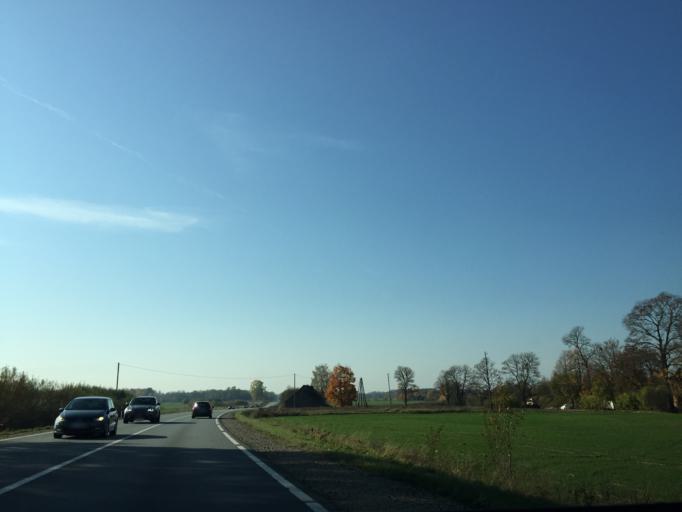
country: LV
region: Dobeles Rajons
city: Dobele
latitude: 56.7073
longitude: 23.1819
